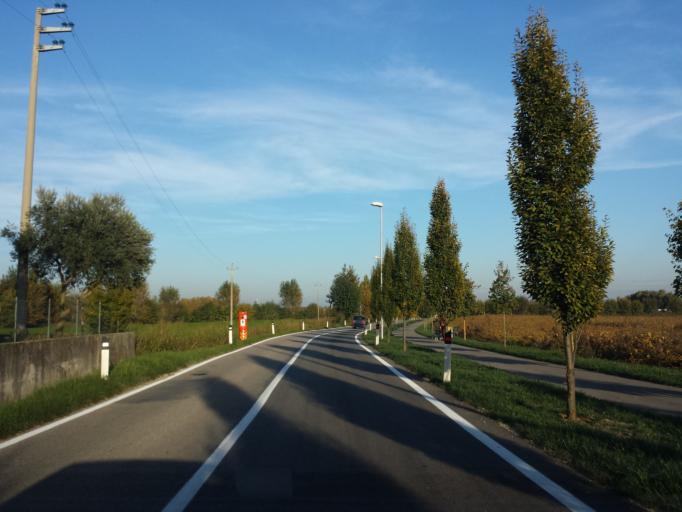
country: IT
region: Veneto
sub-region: Provincia di Vicenza
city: Motta
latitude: 45.5946
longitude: 11.4993
